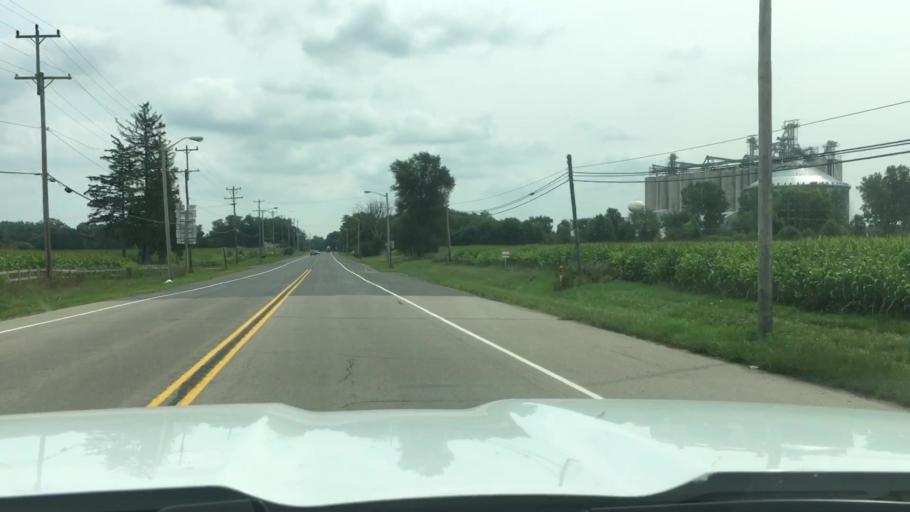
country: US
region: Michigan
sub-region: Ingham County
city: Webberville
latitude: 42.6692
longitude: -84.1978
